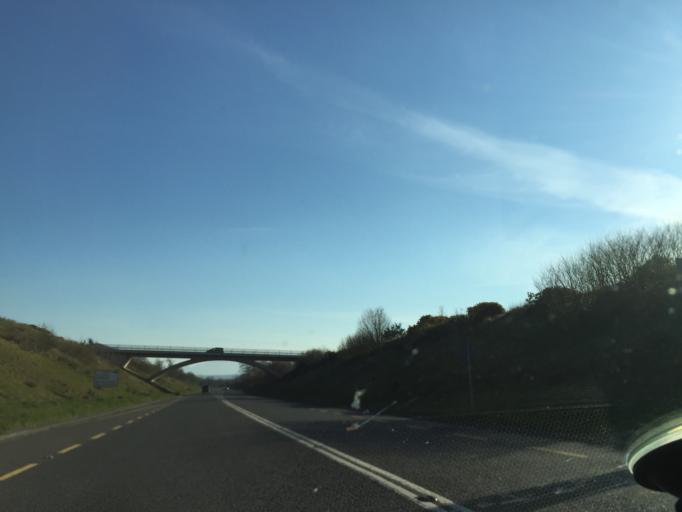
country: IE
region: Munster
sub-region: Ciarrai
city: Castleisland
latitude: 52.2056
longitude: -9.5682
